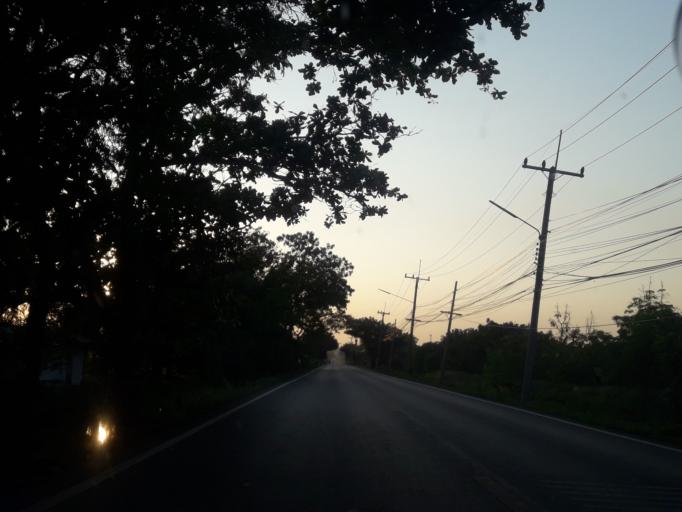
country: TH
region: Pathum Thani
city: Nong Suea
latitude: 14.1317
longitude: 100.8100
